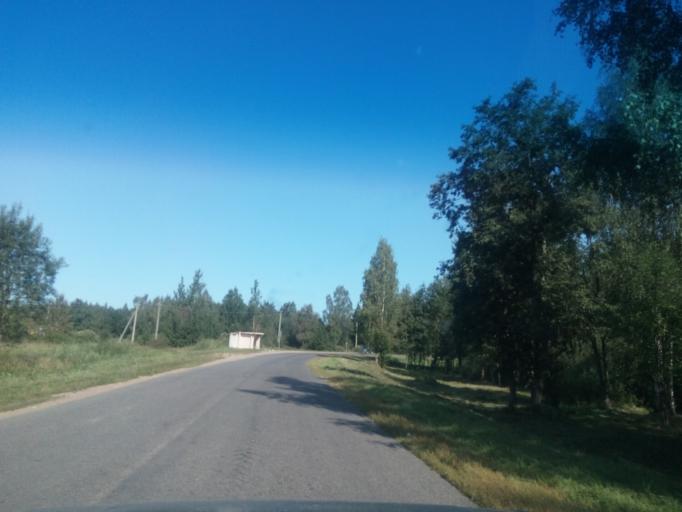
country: BY
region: Vitebsk
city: Dzisna
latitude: 55.6532
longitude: 28.3225
